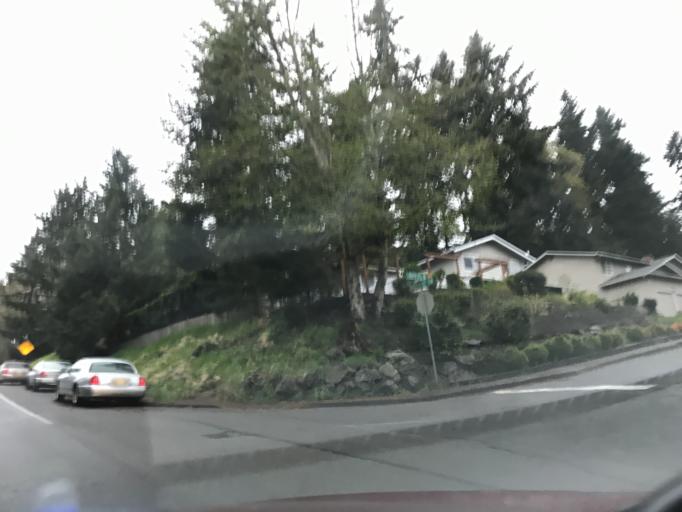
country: US
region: Washington
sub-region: Snohomish County
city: Brier
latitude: 47.7775
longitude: -122.2907
